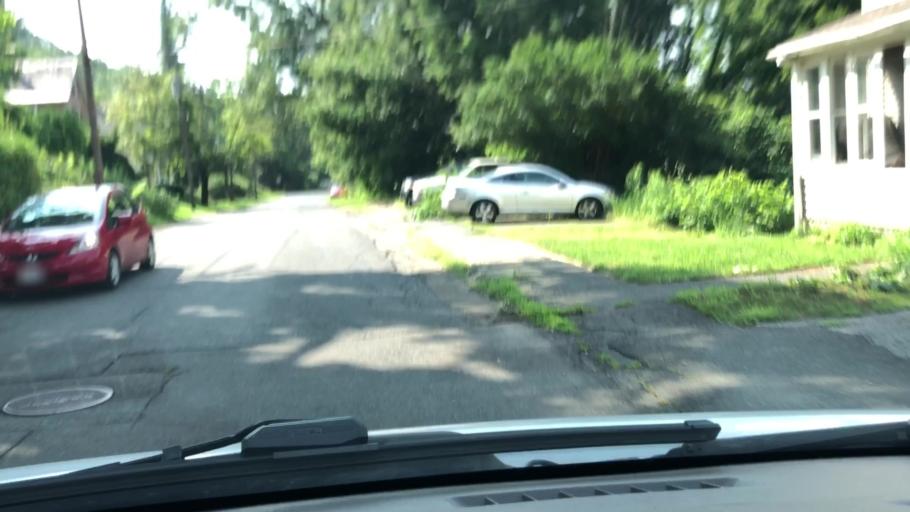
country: US
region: Massachusetts
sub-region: Franklin County
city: Greenfield
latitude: 42.5785
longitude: -72.5957
